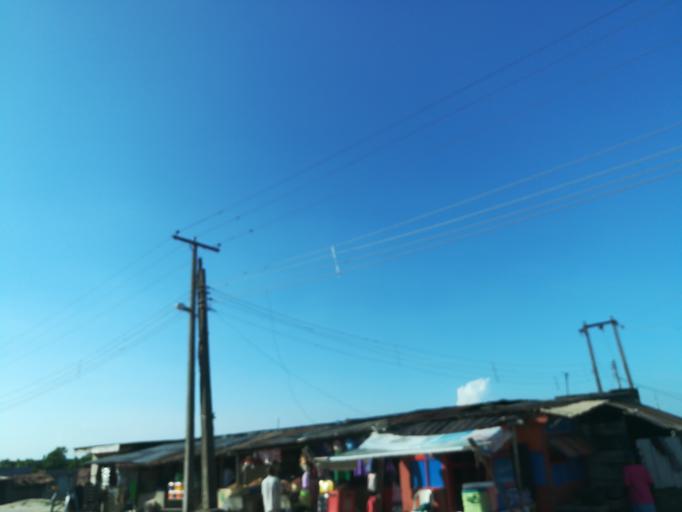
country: NG
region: Lagos
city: Ikorodu
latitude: 6.5388
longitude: 3.5511
